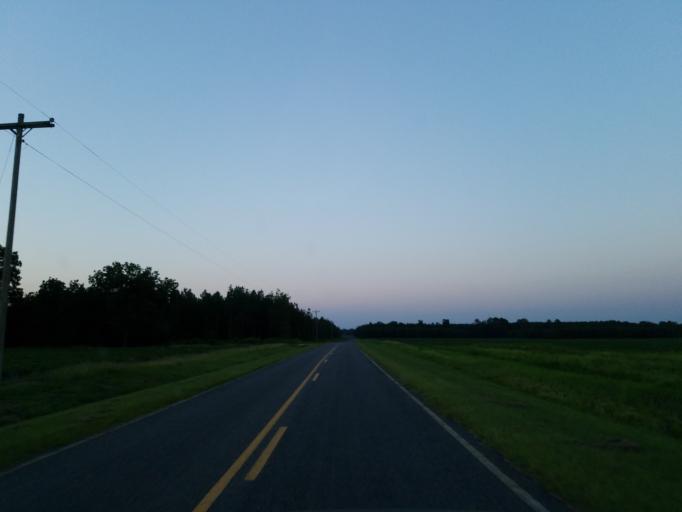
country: US
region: Georgia
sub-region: Dooly County
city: Unadilla
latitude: 32.2089
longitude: -83.7979
